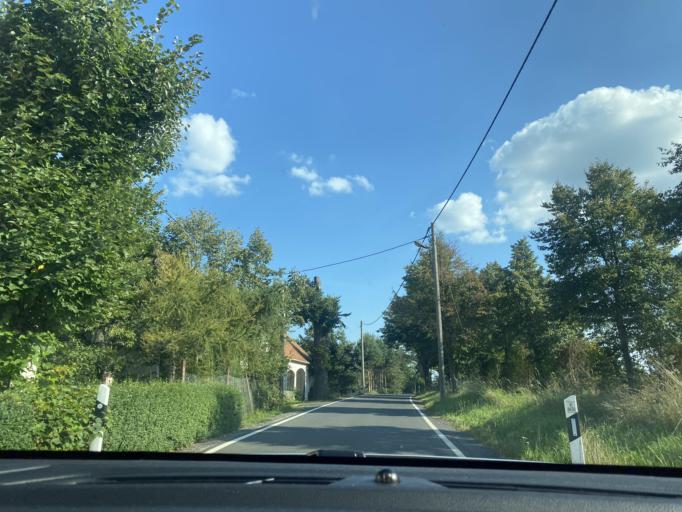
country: DE
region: Saxony
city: Quitzdorf
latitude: 51.2649
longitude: 14.7335
